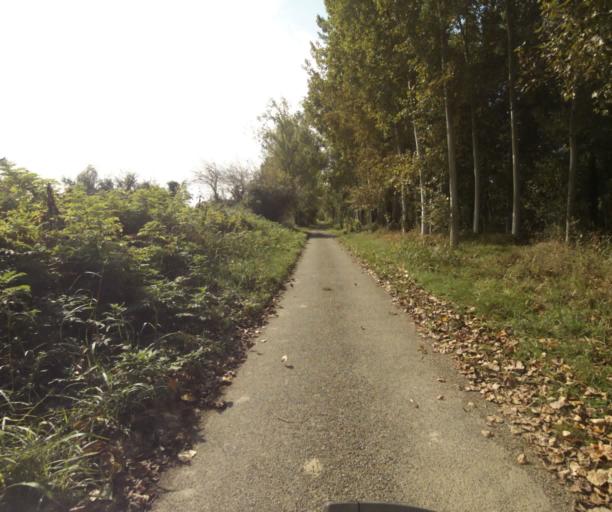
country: FR
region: Midi-Pyrenees
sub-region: Departement du Tarn-et-Garonne
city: Finhan
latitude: 43.8960
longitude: 1.2104
